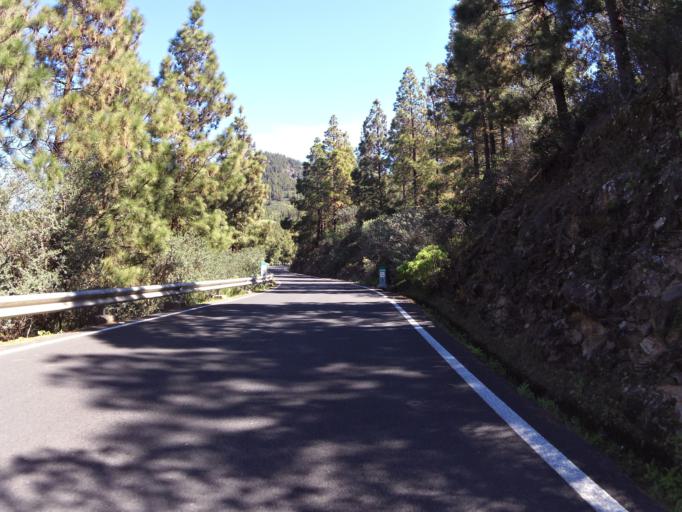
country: ES
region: Canary Islands
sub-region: Provincia de Las Palmas
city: Artenara
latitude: 28.0174
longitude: -15.6722
